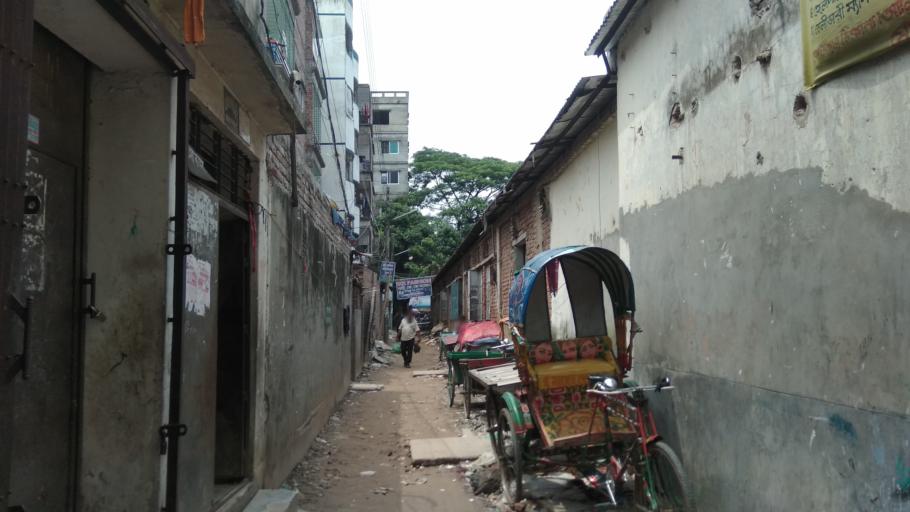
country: BD
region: Dhaka
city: Azimpur
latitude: 23.8030
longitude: 90.3642
